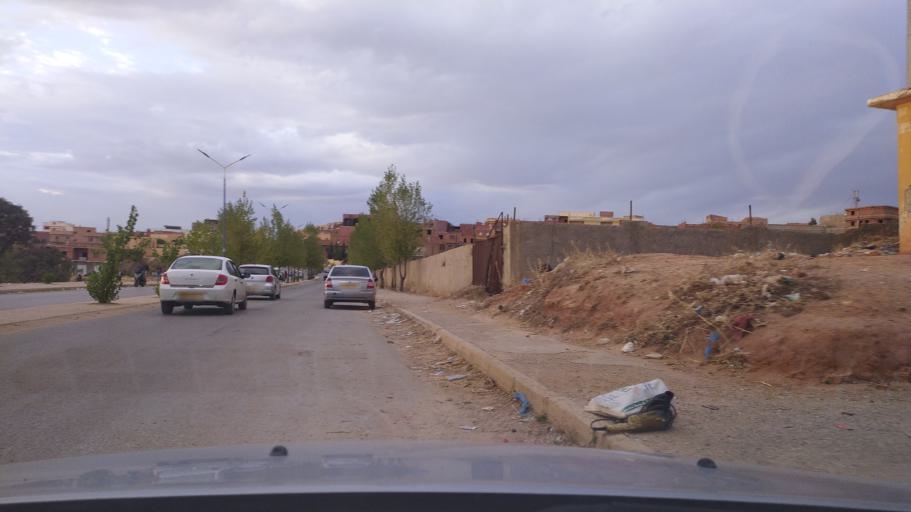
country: DZ
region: Tiaret
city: Frenda
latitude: 35.0577
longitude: 1.0608
